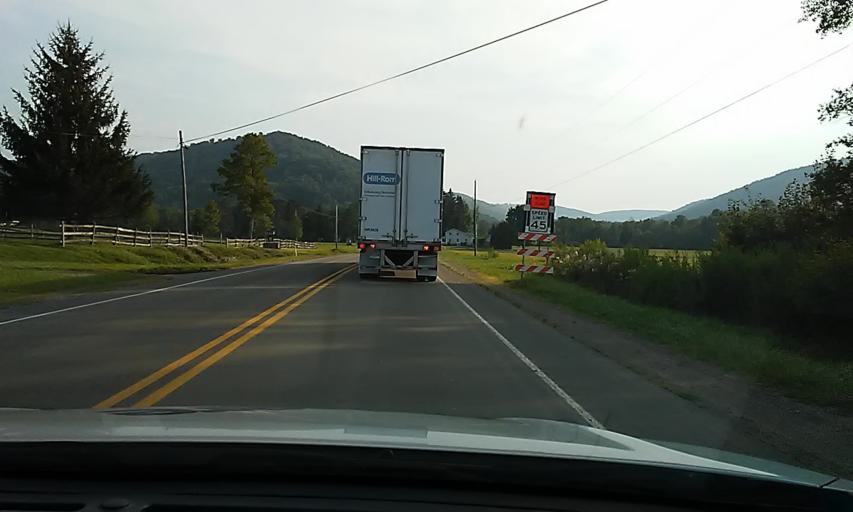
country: US
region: Pennsylvania
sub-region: McKean County
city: Smethport
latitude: 41.7341
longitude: -78.5383
